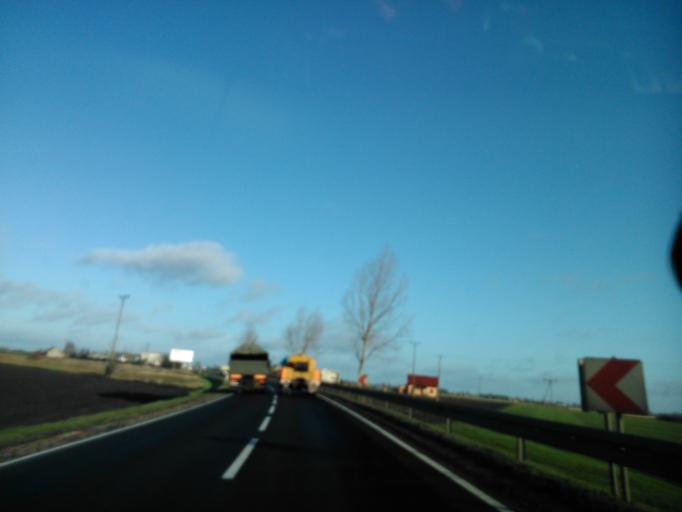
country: PL
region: Kujawsko-Pomorskie
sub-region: Powiat inowroclawski
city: Wierzchoslawice
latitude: 52.8529
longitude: 18.3476
